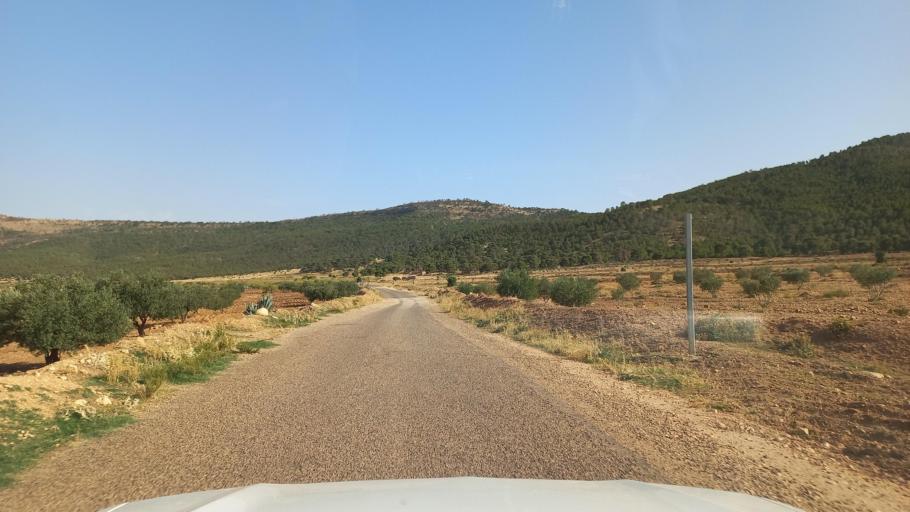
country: TN
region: Al Qasrayn
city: Kasserine
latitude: 35.3380
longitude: 8.8362
